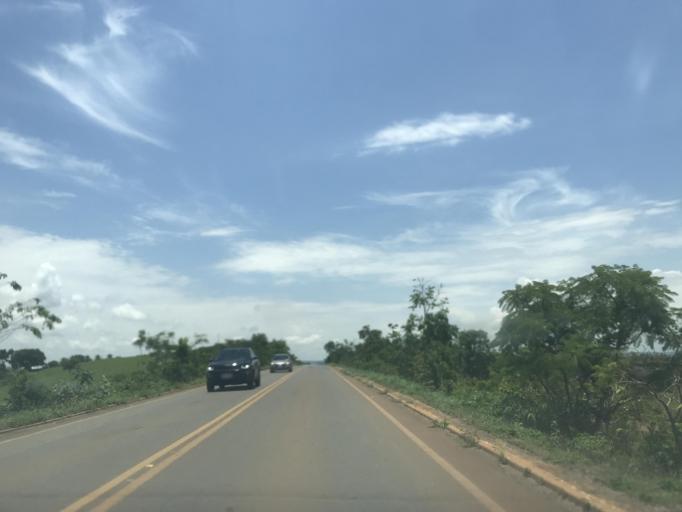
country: BR
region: Goias
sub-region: Vianopolis
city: Vianopolis
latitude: -16.6057
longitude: -48.3499
